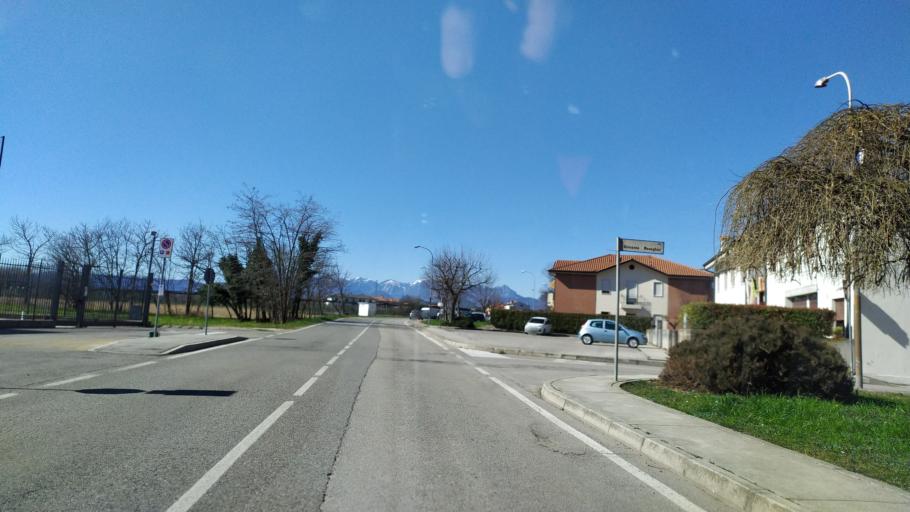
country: IT
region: Veneto
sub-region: Provincia di Vicenza
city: Breganze
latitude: 45.7014
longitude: 11.5608
